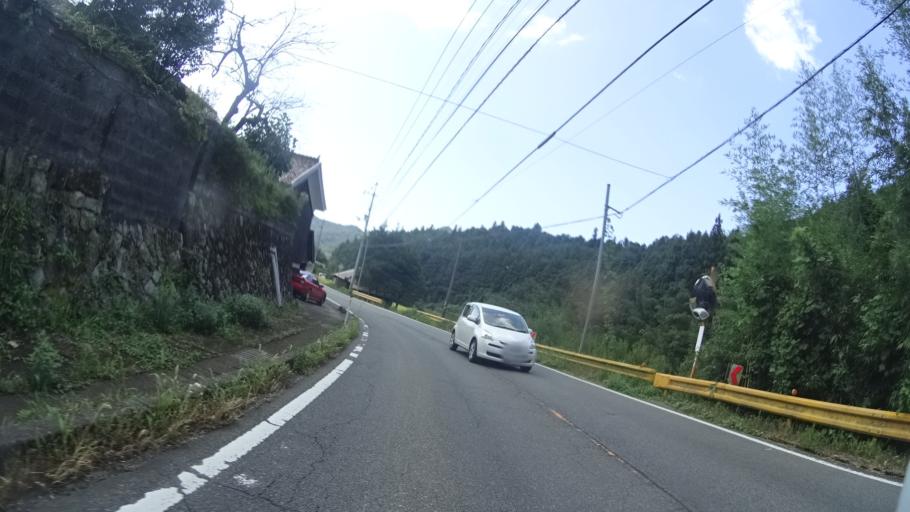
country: JP
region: Yamaguchi
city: Hagi
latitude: 34.4378
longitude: 131.4581
